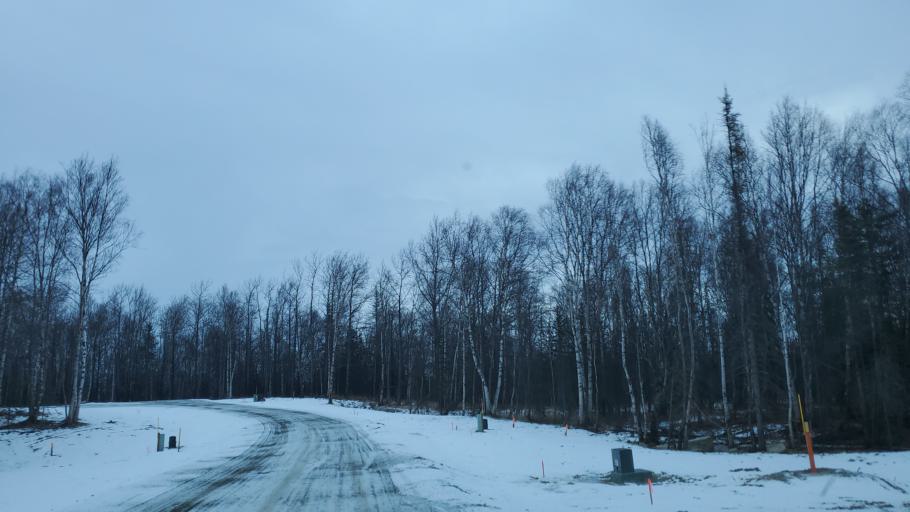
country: US
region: Alaska
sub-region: Matanuska-Susitna Borough
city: Gateway
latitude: 61.6559
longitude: -149.2298
